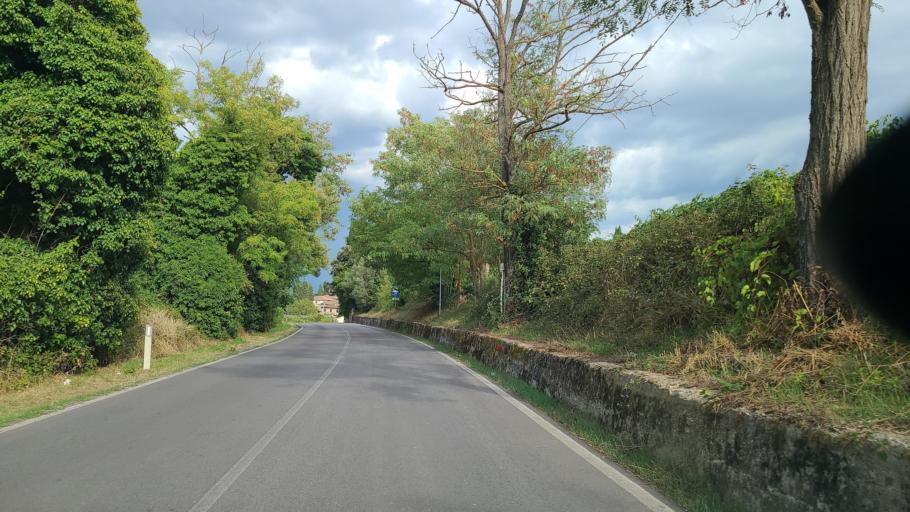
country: IT
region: Tuscany
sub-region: Provincia di Siena
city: San Gimignano
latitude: 43.4780
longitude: 11.0202
